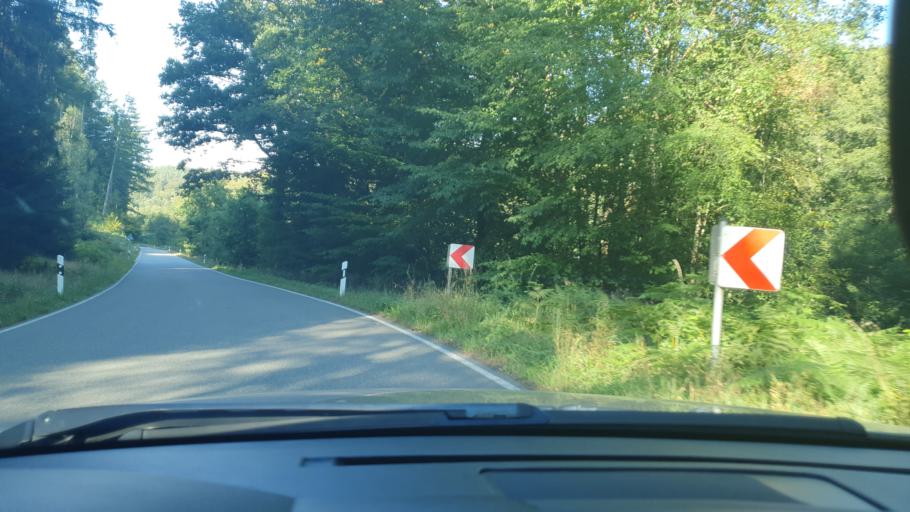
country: DE
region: Rheinland-Pfalz
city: Trippstadt
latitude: 49.3322
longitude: 7.7662
